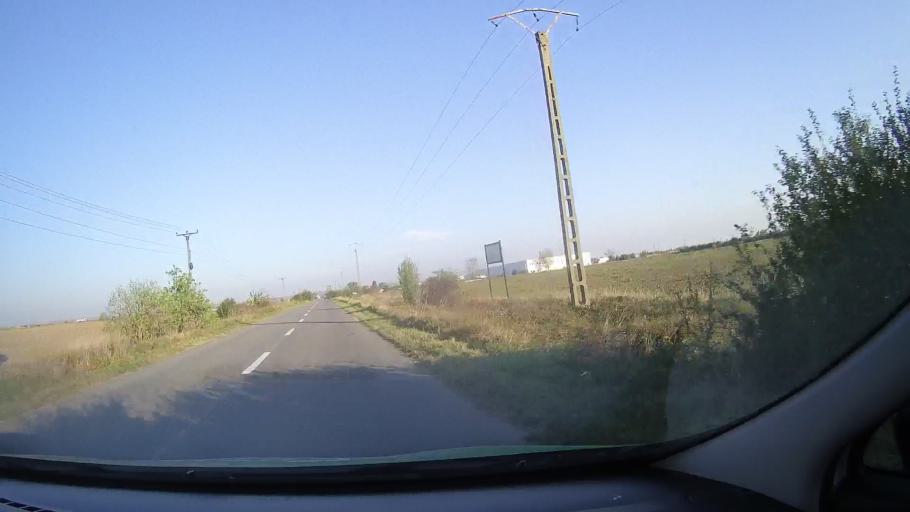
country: RO
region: Bihor
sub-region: Comuna Bors
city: Santion
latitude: 47.1147
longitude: 21.8416
